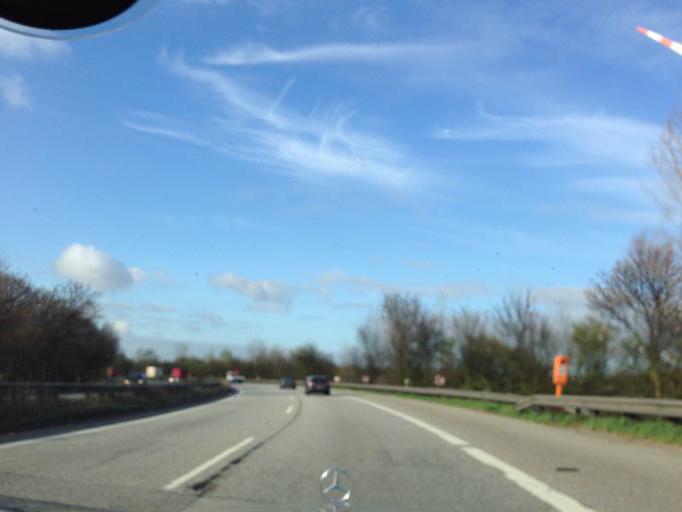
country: DE
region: Hamburg
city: Rothenburgsort
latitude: 53.5085
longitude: 10.0359
